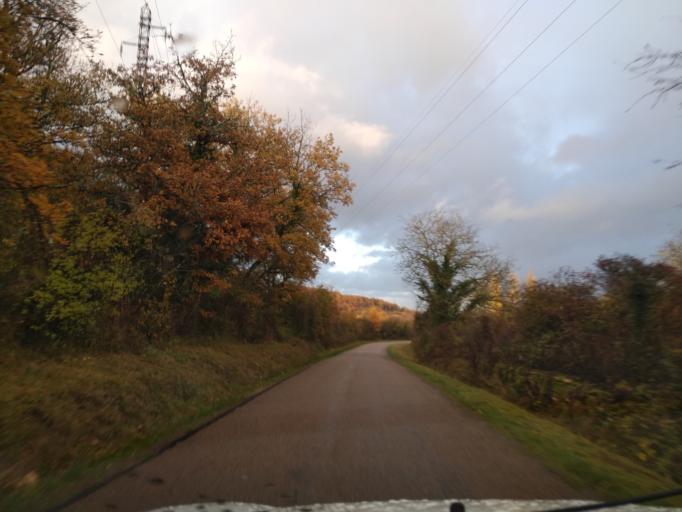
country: FR
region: Bourgogne
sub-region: Departement de Saone-et-Loire
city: Rully
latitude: 46.8873
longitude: 4.7202
